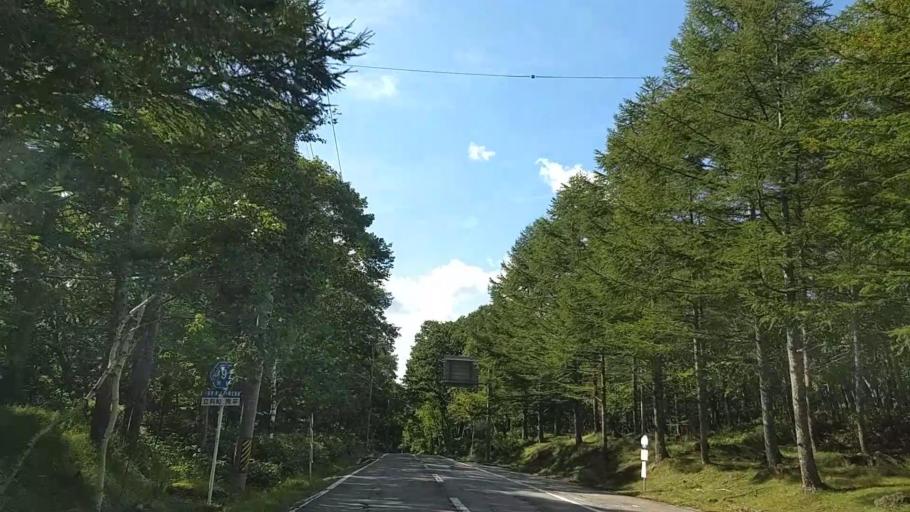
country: JP
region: Nagano
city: Chino
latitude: 36.0950
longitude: 138.2767
